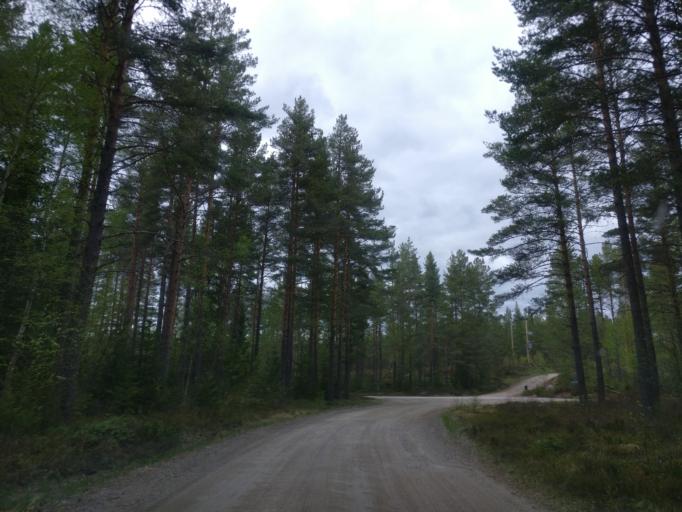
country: SE
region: Gaevleborg
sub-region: Soderhamns Kommun
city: Marielund
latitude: 61.4647
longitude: 17.0830
